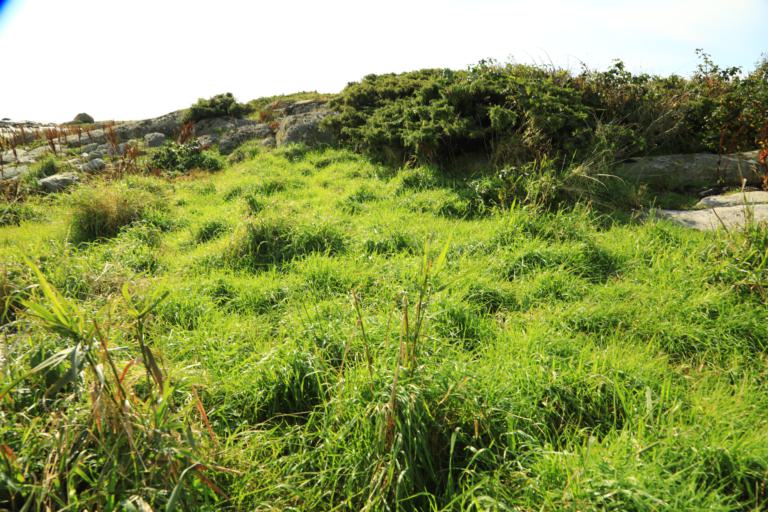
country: SE
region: Halland
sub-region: Varbergs Kommun
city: Varberg
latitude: 57.1209
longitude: 12.1931
